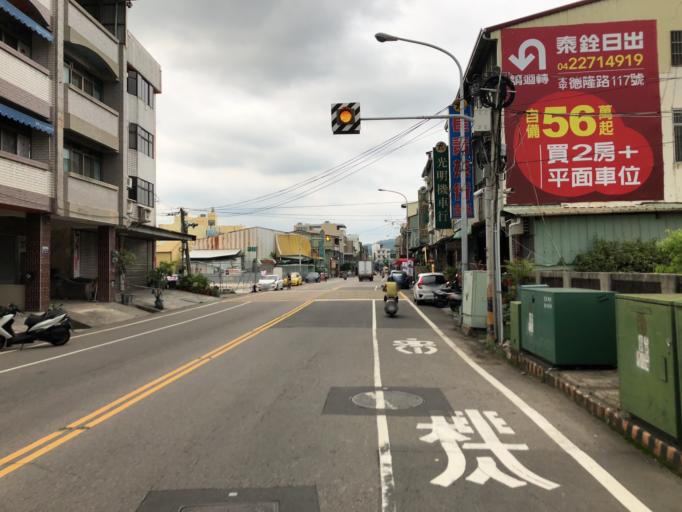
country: TW
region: Taiwan
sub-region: Taichung City
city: Taichung
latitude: 24.1092
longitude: 120.7298
